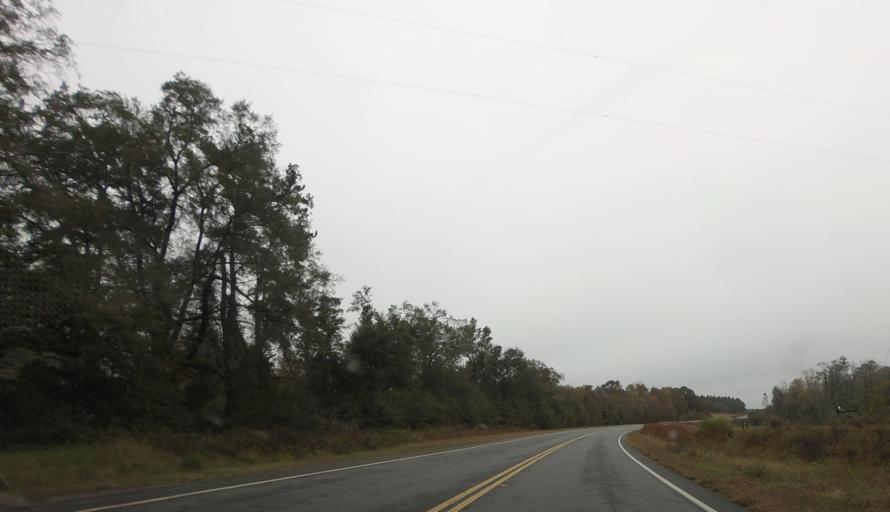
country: US
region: Georgia
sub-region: Marion County
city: Buena Vista
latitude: 32.3732
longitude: -84.4554
